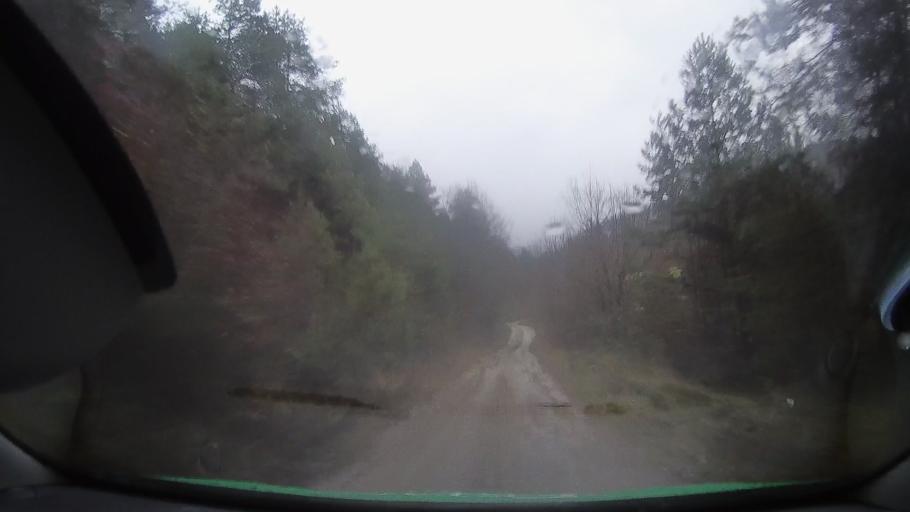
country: RO
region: Alba
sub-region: Comuna Avram Iancu
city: Avram Iancu
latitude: 46.3105
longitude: 22.7798
